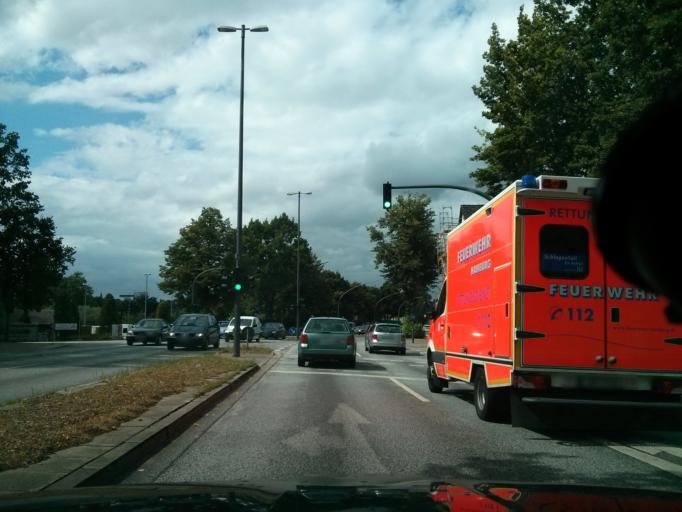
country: DE
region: Hamburg
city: Eidelstedt
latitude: 53.5689
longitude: 9.8802
